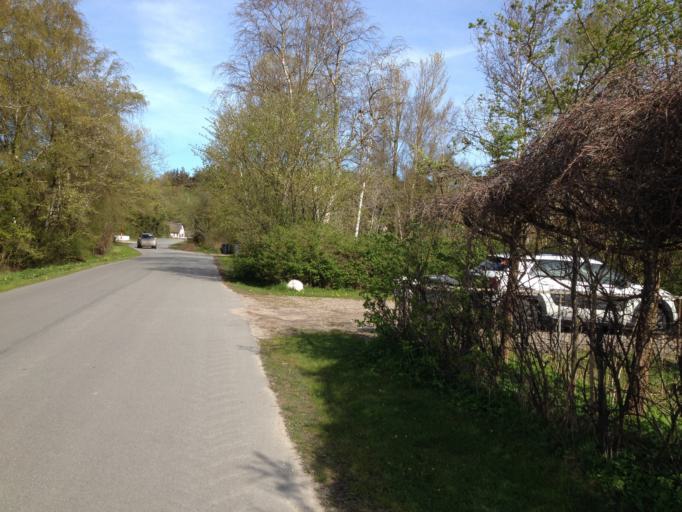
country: DK
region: Capital Region
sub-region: Halsnaes Kommune
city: Hundested
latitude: 55.9460
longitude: 11.9011
